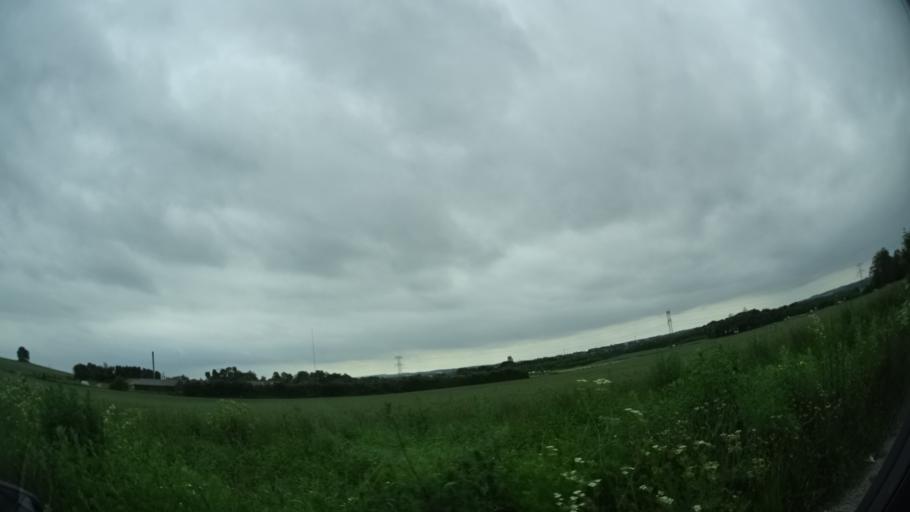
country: DK
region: Central Jutland
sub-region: Arhus Kommune
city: Kolt
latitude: 56.0997
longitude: 10.0628
